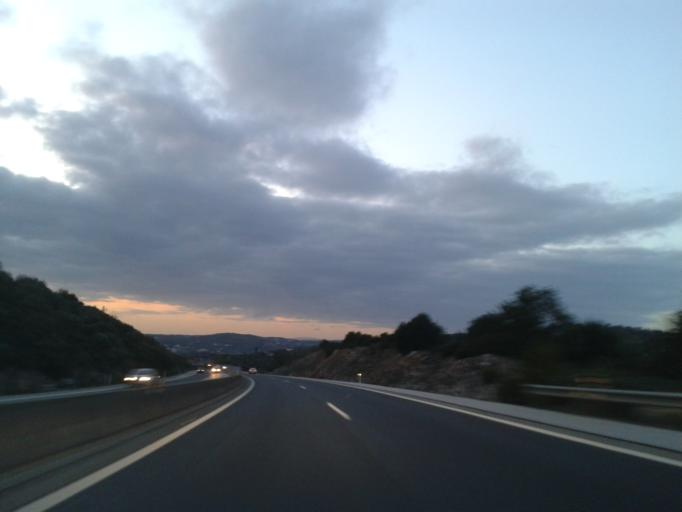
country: PT
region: Faro
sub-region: Loule
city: Boliqueime
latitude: 37.1594
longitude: -8.1834
